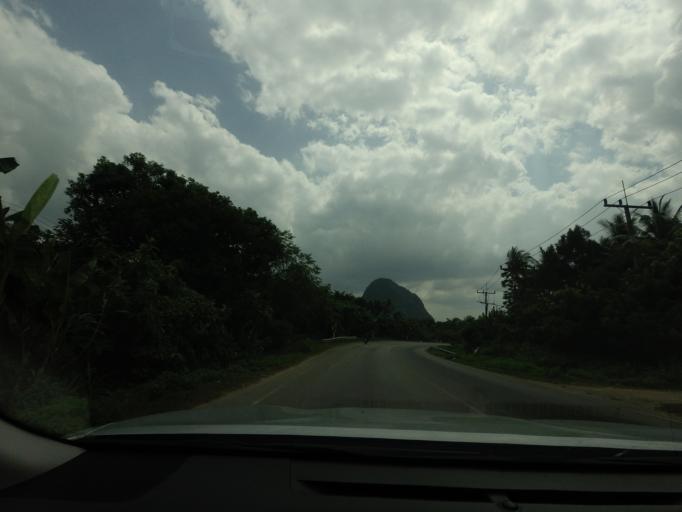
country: TH
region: Phangnga
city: Ban Ao Nang
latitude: 8.1164
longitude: 98.8019
